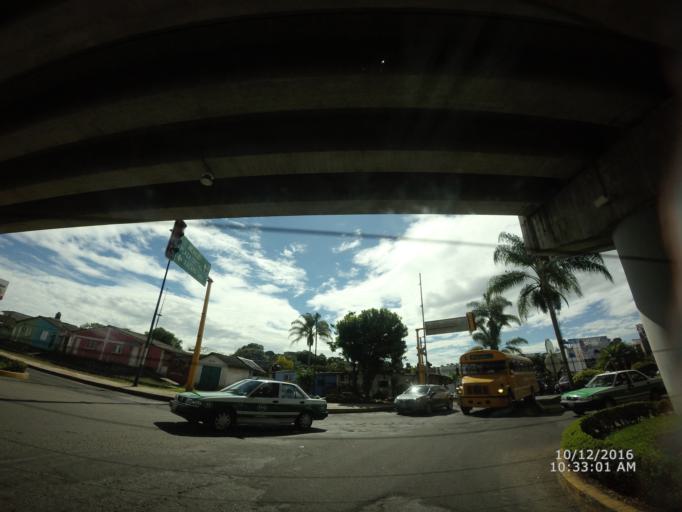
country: TR
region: Sivas
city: Celalli
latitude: 39.6590
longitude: 37.5064
